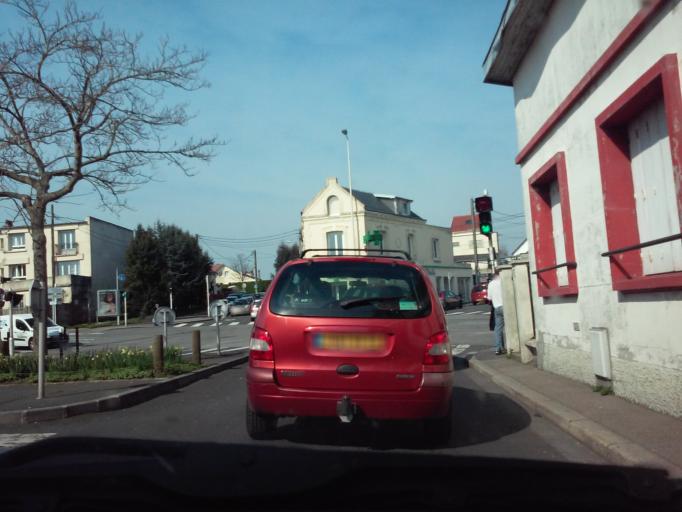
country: FR
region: Haute-Normandie
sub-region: Departement de la Seine-Maritime
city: Le Havre
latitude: 49.5087
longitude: 0.1081
